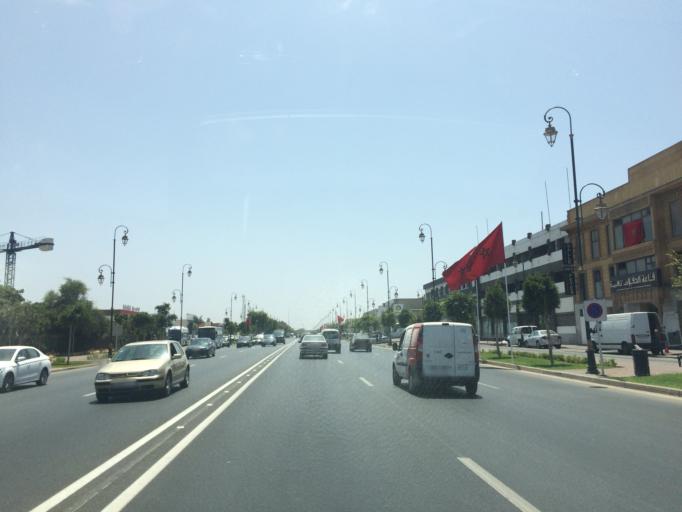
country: MA
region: Rabat-Sale-Zemmour-Zaer
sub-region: Rabat
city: Rabat
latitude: 33.9874
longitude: -6.8689
